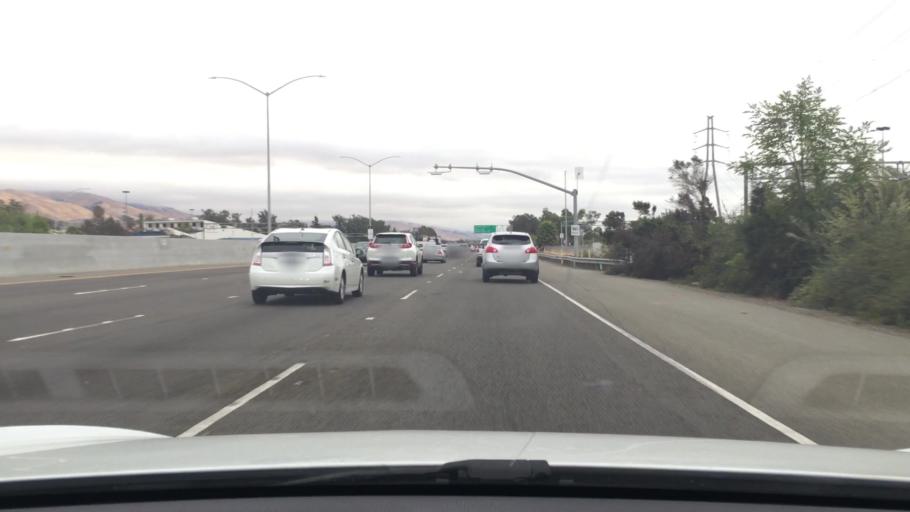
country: US
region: California
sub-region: Alameda County
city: Fremont
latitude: 37.5011
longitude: -121.9597
